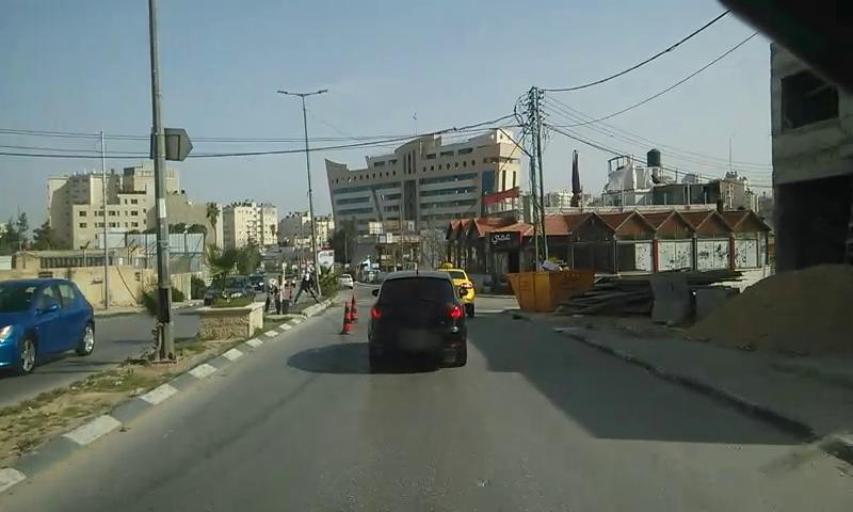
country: PS
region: West Bank
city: Surda
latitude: 31.9245
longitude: 35.2090
